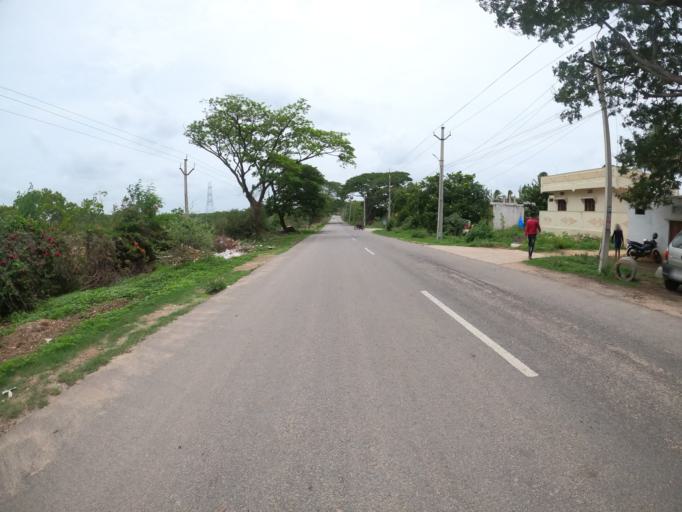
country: IN
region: Telangana
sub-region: Hyderabad
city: Hyderabad
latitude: 17.3425
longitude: 78.3608
